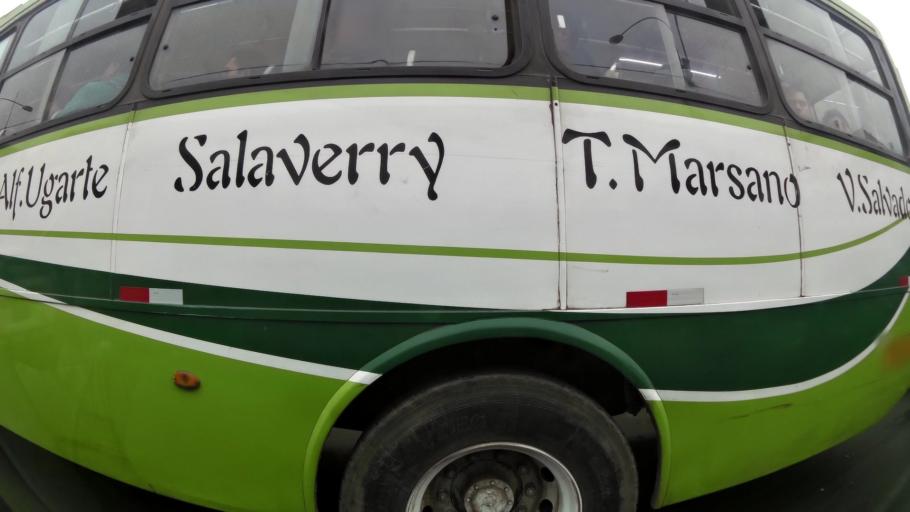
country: PE
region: Lima
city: Lima
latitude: -12.0465
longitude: -77.0438
